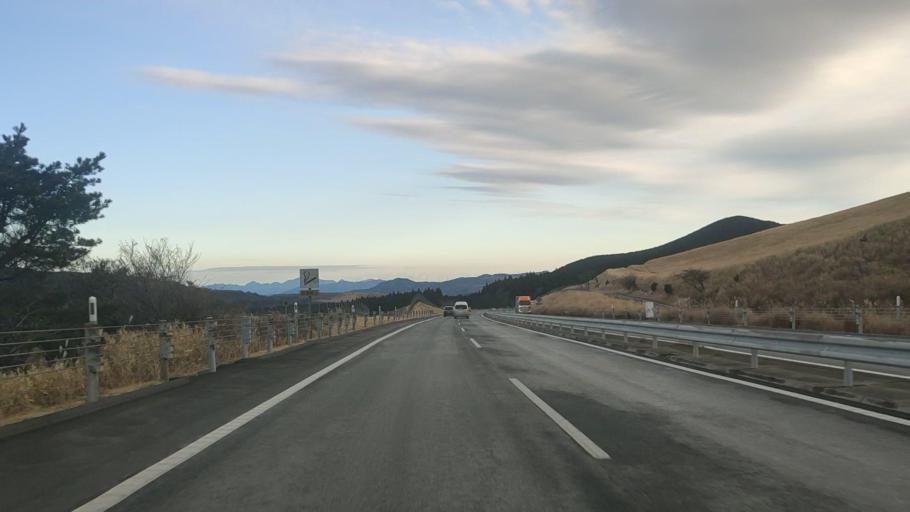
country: JP
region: Oita
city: Beppu
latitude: 33.3278
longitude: 131.4180
